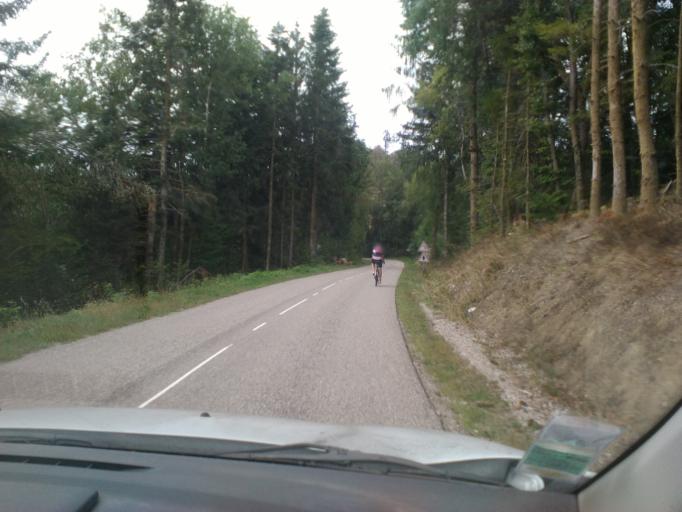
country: FR
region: Lorraine
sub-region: Departement des Vosges
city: Le Tholy
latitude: 48.1118
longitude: 6.7517
